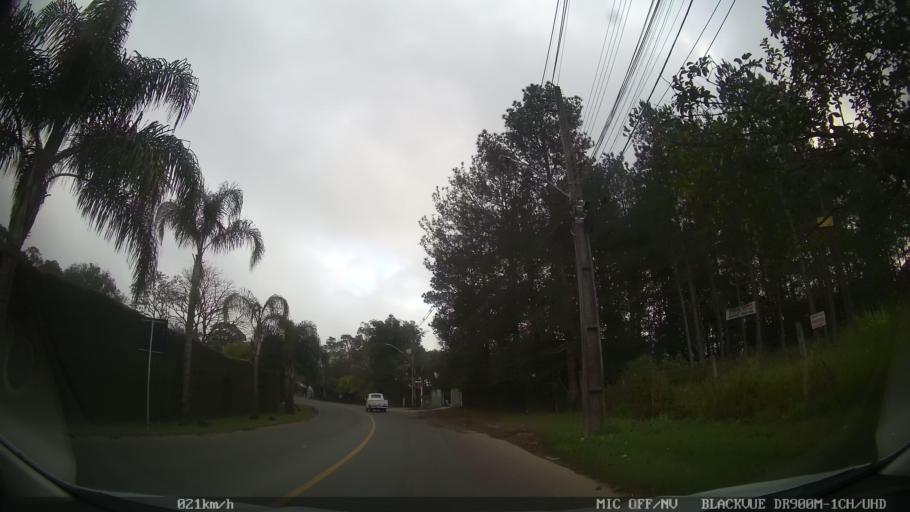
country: BR
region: Parana
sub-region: Almirante Tamandare
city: Almirante Tamandare
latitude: -25.3726
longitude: -49.3197
